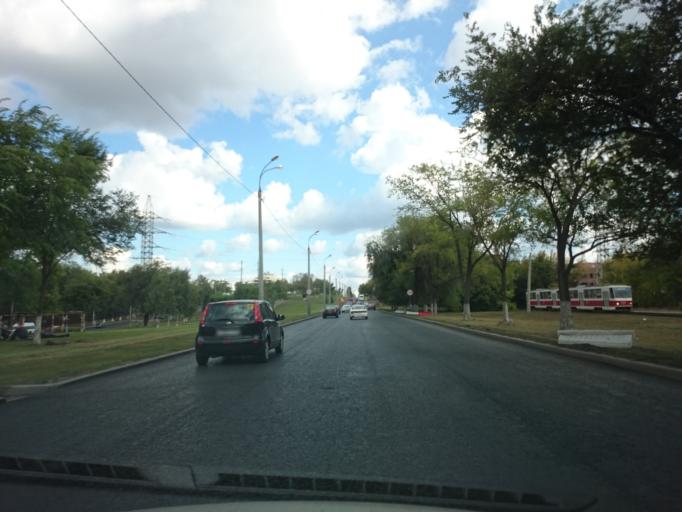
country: RU
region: Samara
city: Samara
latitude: 53.2250
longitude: 50.1721
